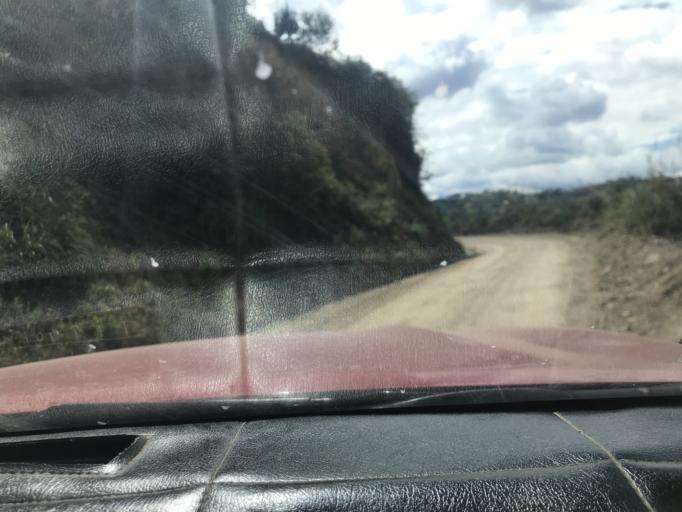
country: PE
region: Cajamarca
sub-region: Provincia de Chota
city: Querocoto
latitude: -6.3484
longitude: -79.0350
